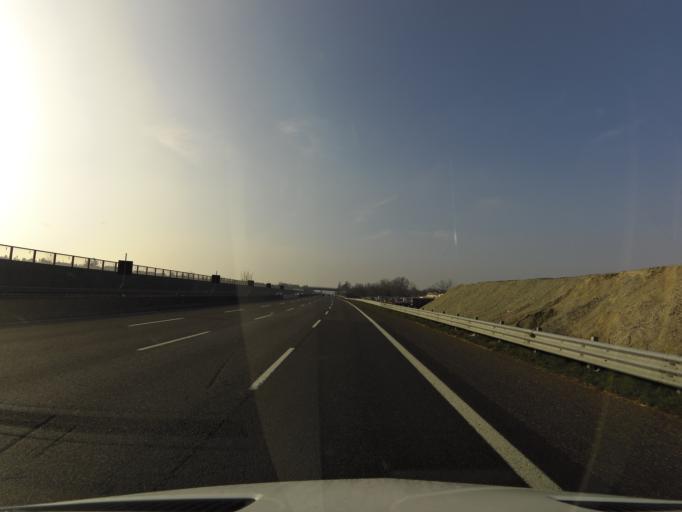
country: IT
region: Emilia-Romagna
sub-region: Provincia di Modena
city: San Cesario sul Panaro
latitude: 44.5653
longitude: 11.0423
